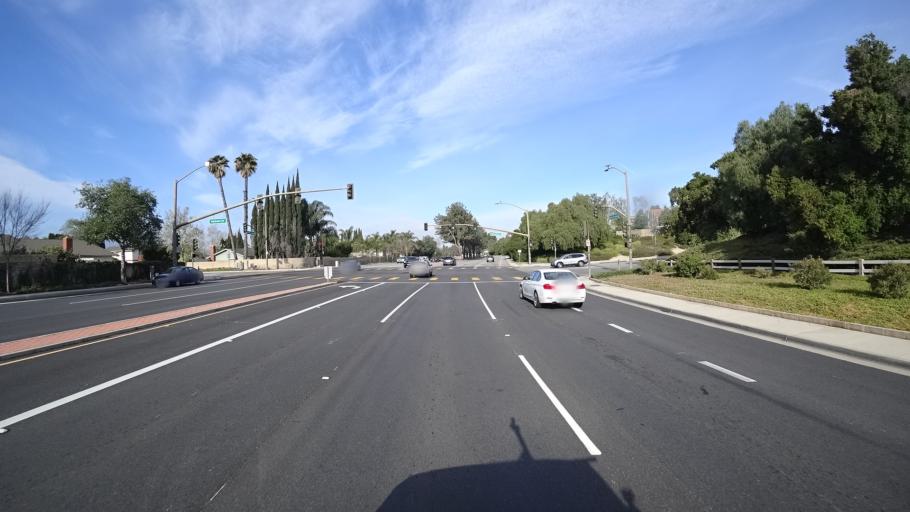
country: US
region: California
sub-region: Ventura County
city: Thousand Oaks
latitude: 34.2119
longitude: -118.8353
